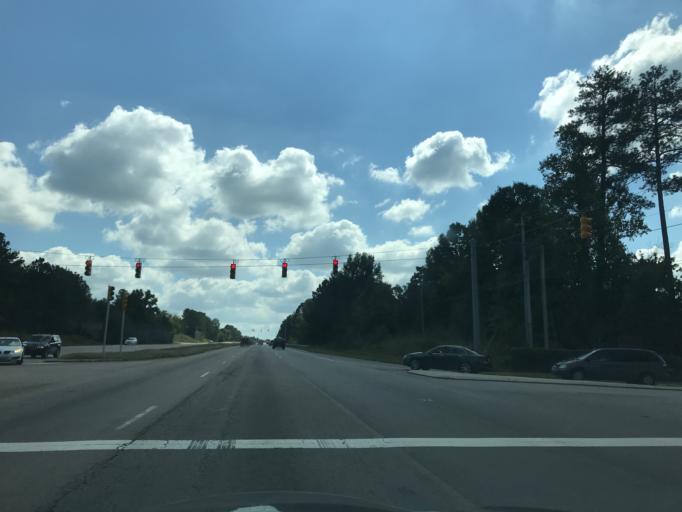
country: US
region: North Carolina
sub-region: Wake County
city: Wake Forest
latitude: 35.9574
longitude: -78.5418
